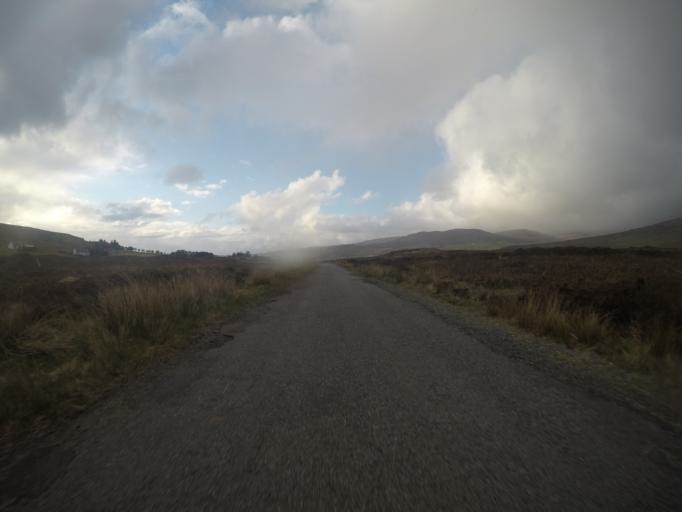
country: GB
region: Scotland
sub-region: Highland
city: Isle of Skye
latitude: 57.4631
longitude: -6.2969
